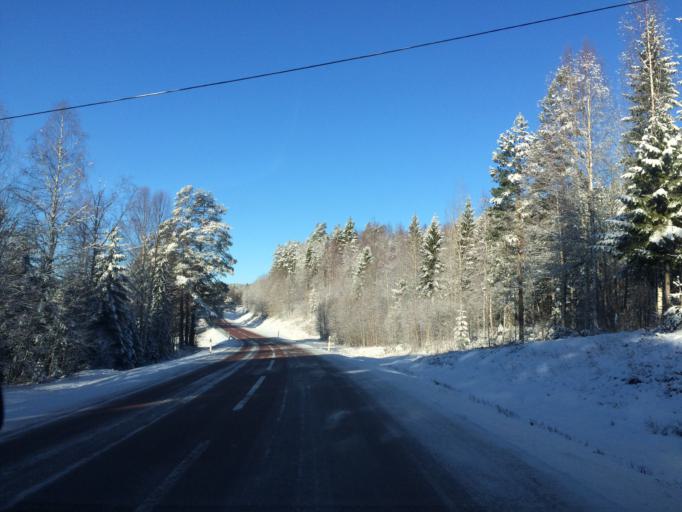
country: SE
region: Dalarna
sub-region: Vansbro Kommun
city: Vansbro
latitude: 60.8552
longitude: 14.2301
